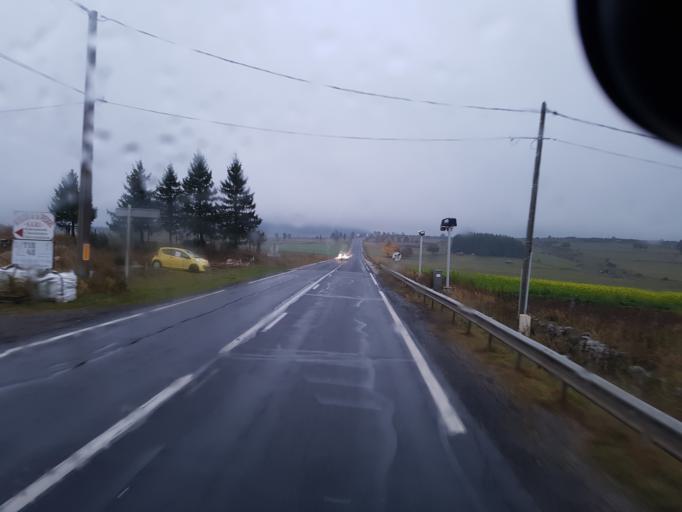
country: FR
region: Languedoc-Roussillon
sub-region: Departement de la Lozere
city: Langogne
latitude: 44.8468
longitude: 3.8540
